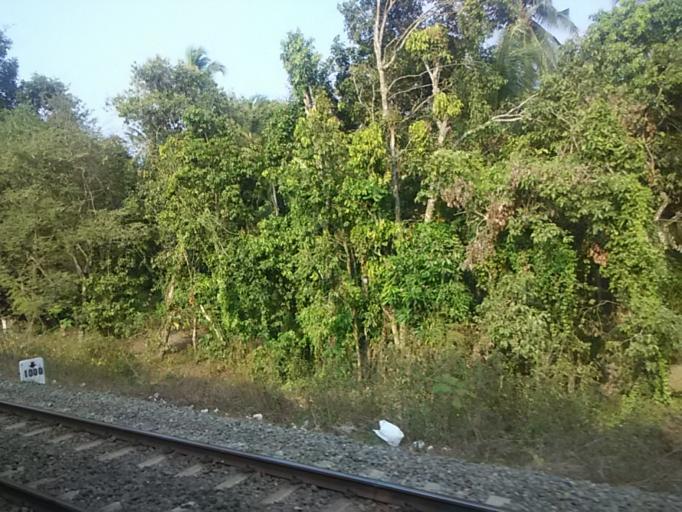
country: IN
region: Kerala
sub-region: Malappuram
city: Pariyapuram
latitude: 11.0648
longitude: 75.8559
